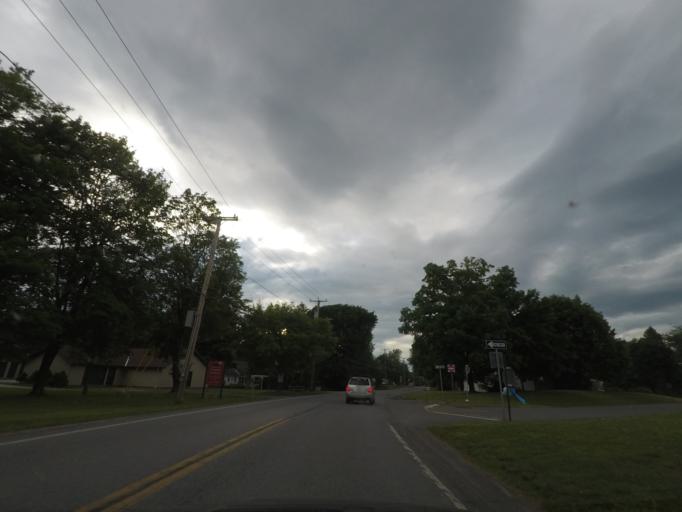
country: US
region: New York
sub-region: Dutchess County
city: Pine Plains
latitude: 41.9812
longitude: -73.6632
